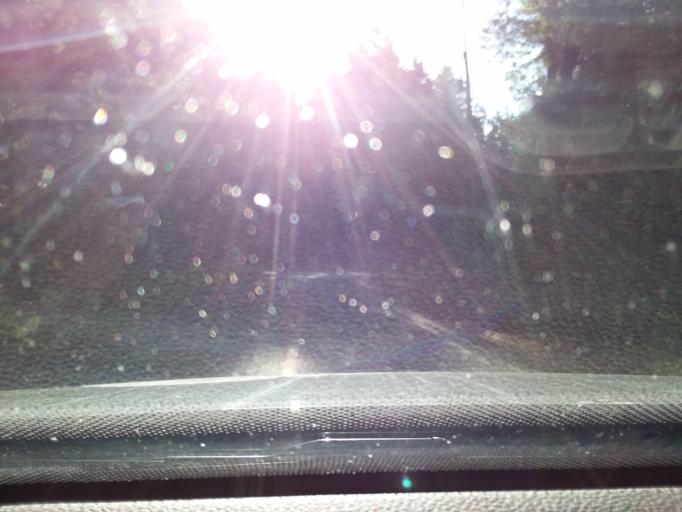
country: CA
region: British Columbia
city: North Cowichan
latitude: 48.9648
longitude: -123.5512
